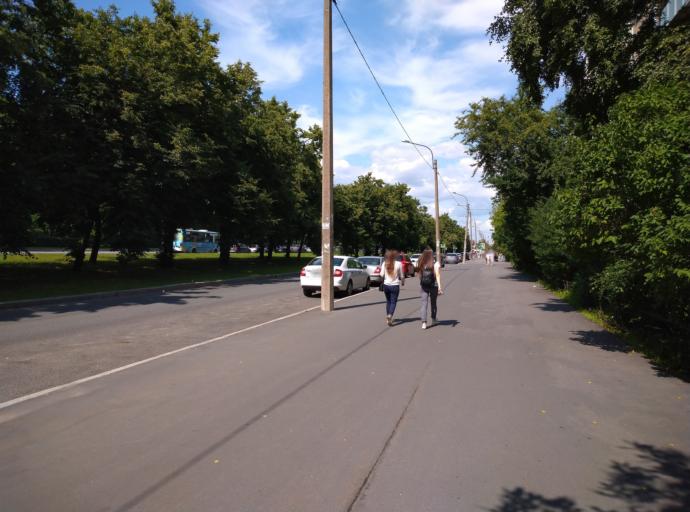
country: RU
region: St.-Petersburg
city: Kupchino
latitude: 59.8605
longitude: 30.3379
